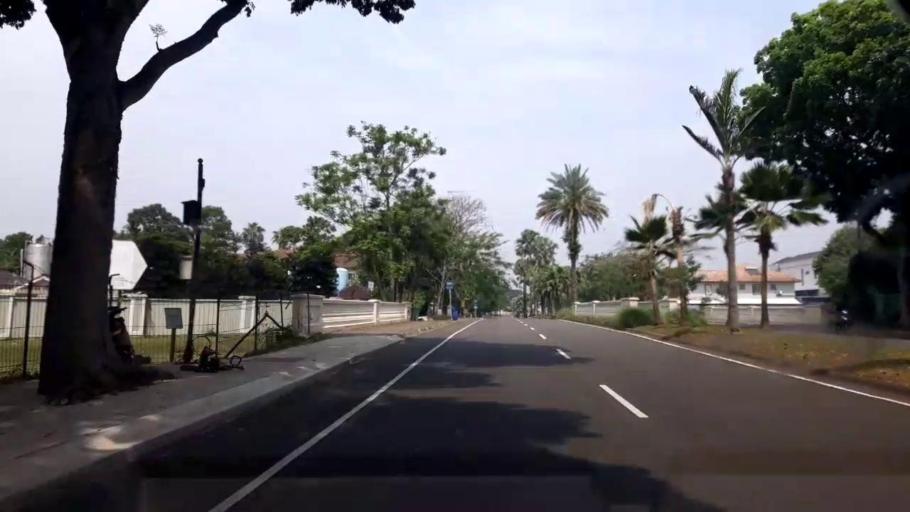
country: ID
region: Banten
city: Curug
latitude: -6.2401
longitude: 106.6011
